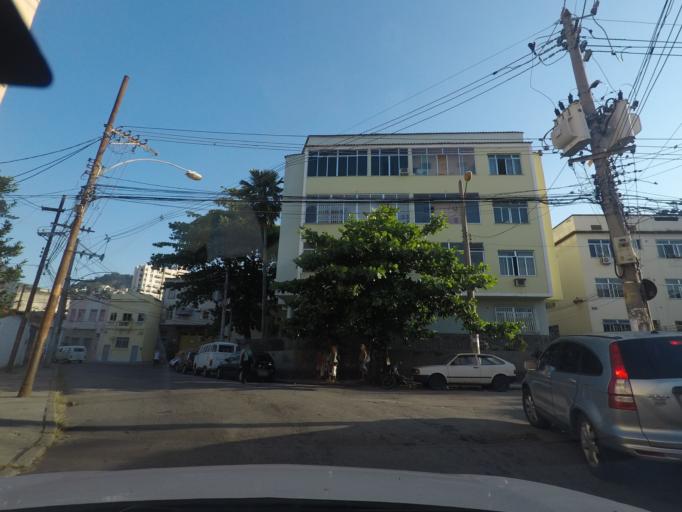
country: BR
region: Rio de Janeiro
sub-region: Rio De Janeiro
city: Rio de Janeiro
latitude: -22.9166
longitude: -43.1962
